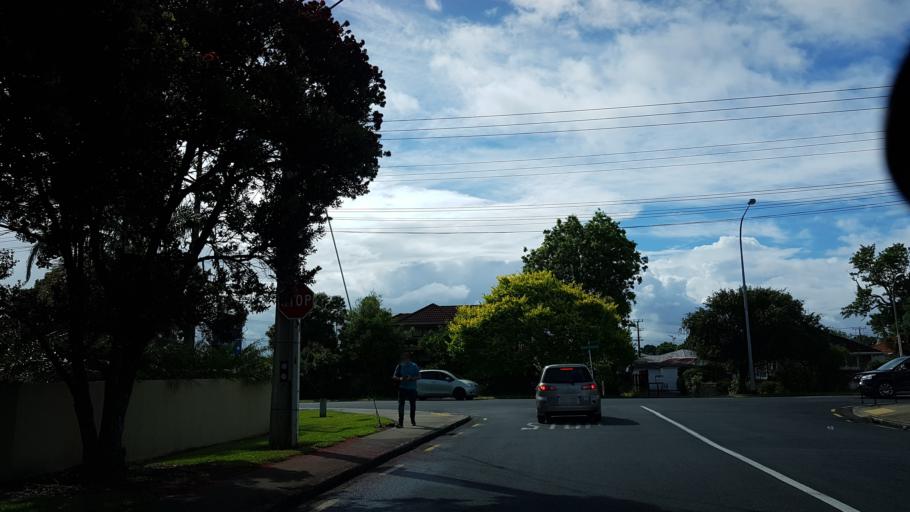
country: NZ
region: Auckland
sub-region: Auckland
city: North Shore
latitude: -36.7945
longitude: 174.7442
